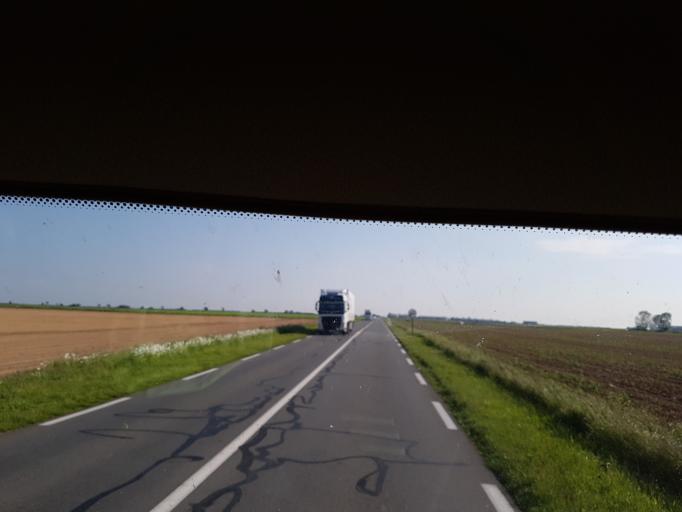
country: FR
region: Picardie
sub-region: Departement de la Somme
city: Abbeville
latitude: 50.1479
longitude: 1.8488
